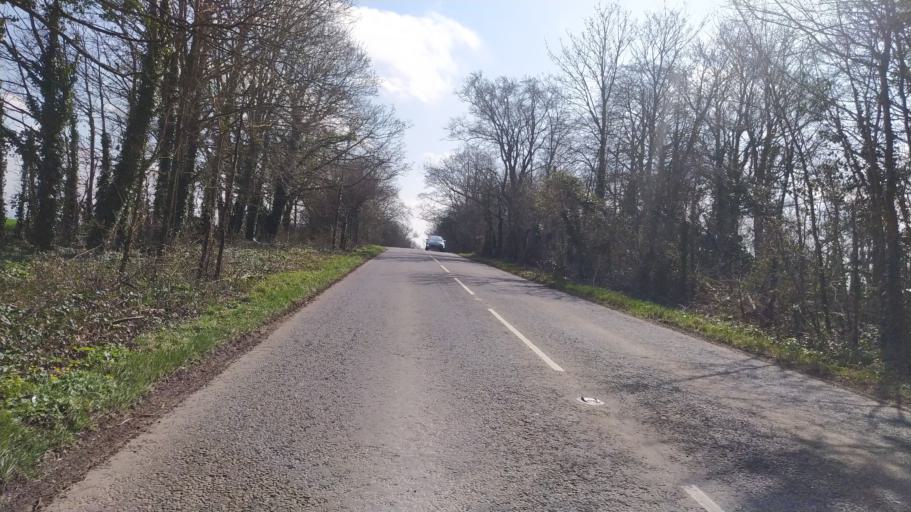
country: GB
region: England
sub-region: Somerset
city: Ilchester
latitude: 51.0207
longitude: -2.6894
